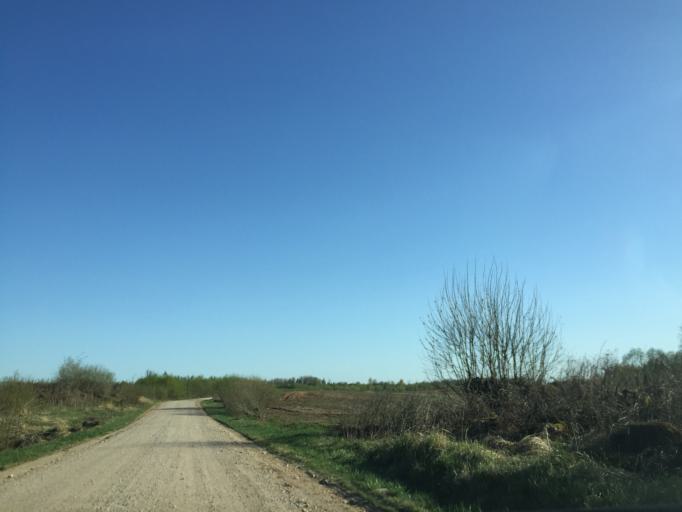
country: LV
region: Ergli
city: Ergli
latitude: 56.9025
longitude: 25.4959
